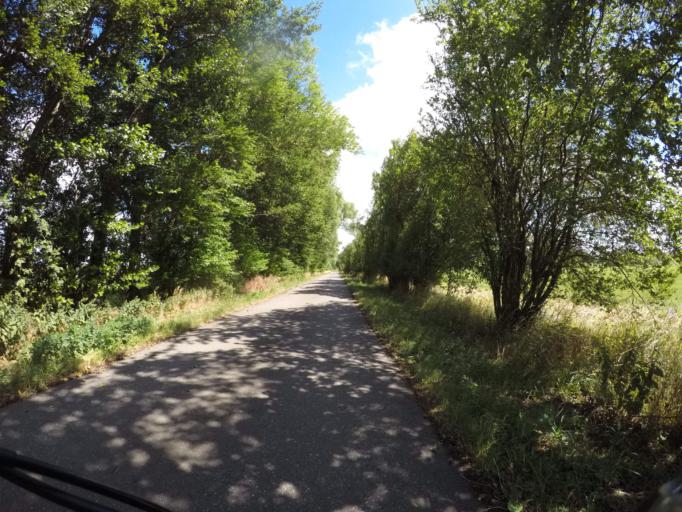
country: DE
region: Lower Saxony
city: Hitzacker
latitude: 53.2054
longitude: 10.9956
